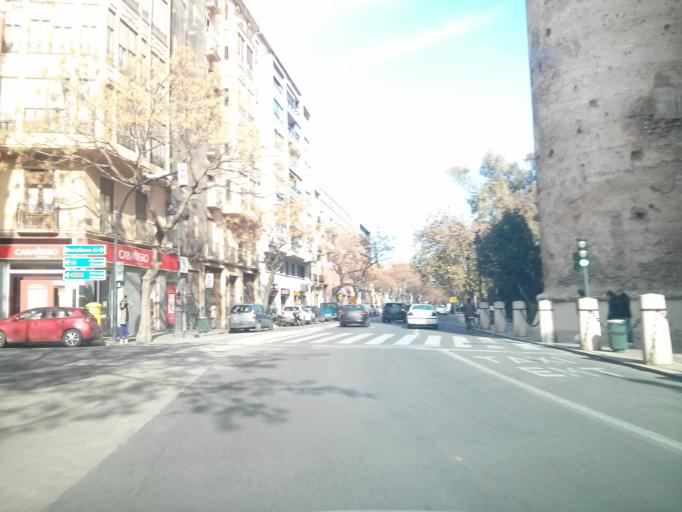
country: ES
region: Valencia
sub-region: Provincia de Valencia
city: Valencia
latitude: 39.4755
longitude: -0.3839
